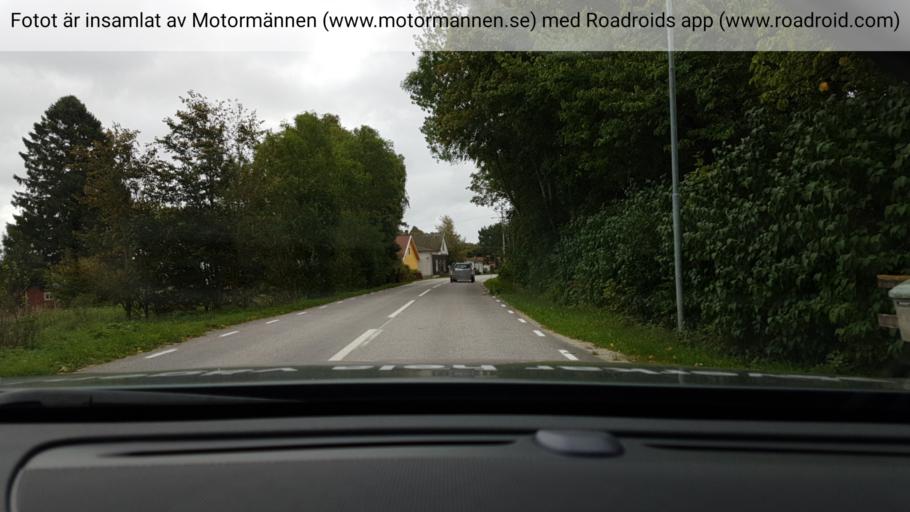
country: SE
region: Gotland
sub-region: Gotland
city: Hemse
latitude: 57.1875
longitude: 18.2454
